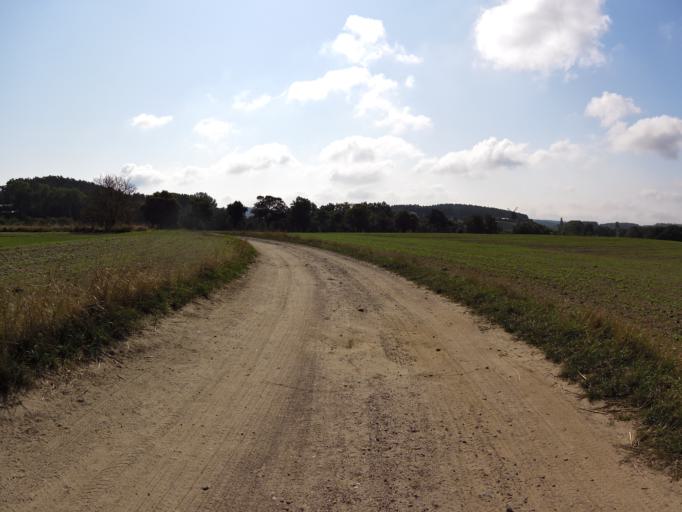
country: DE
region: Mecklenburg-Vorpommern
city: Loddin
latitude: 53.9667
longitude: 14.0625
